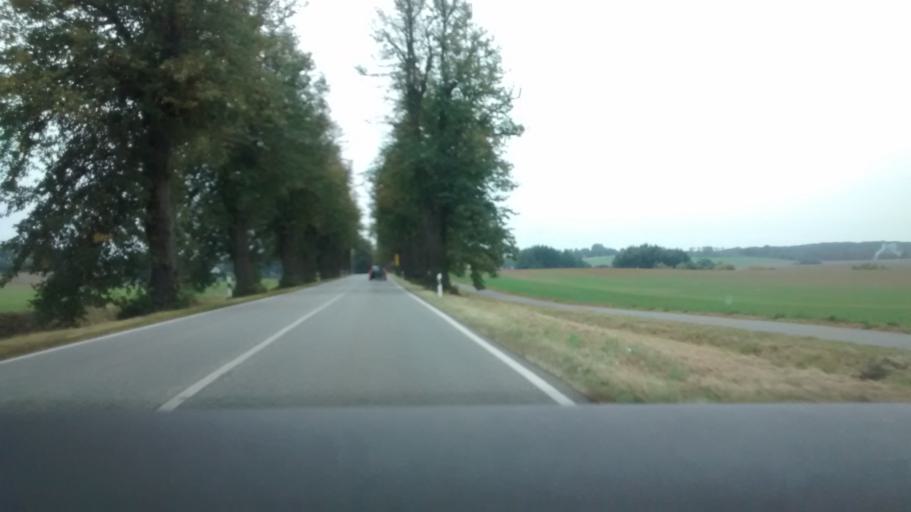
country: DE
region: Mecklenburg-Vorpommern
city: Mecklenburg
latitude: 53.8309
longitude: 11.4563
